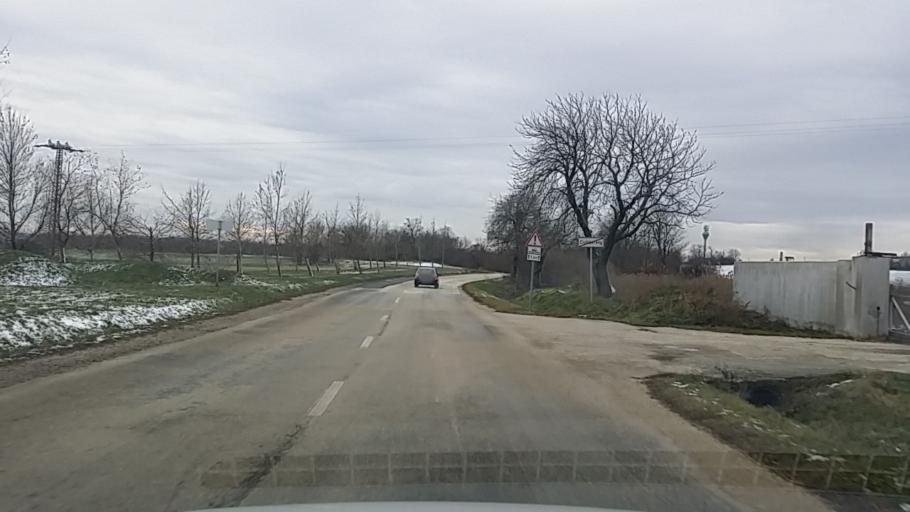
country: HU
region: Fejer
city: Fehervarcsurgo
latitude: 47.3447
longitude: 18.3268
